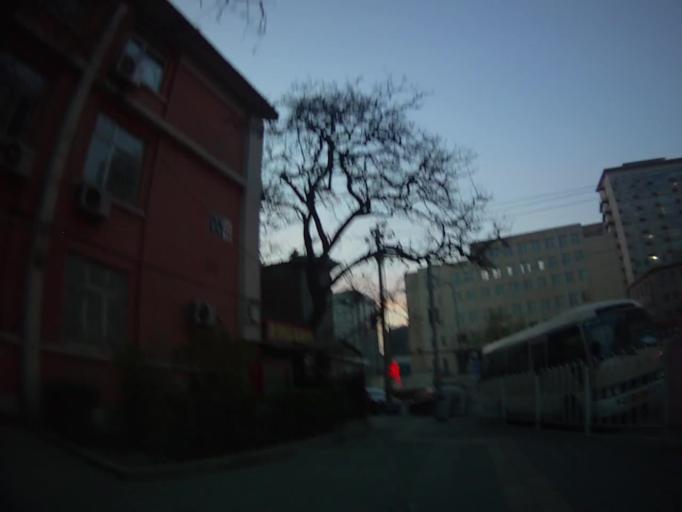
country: CN
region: Beijing
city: Longtan
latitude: 39.8906
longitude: 116.4335
